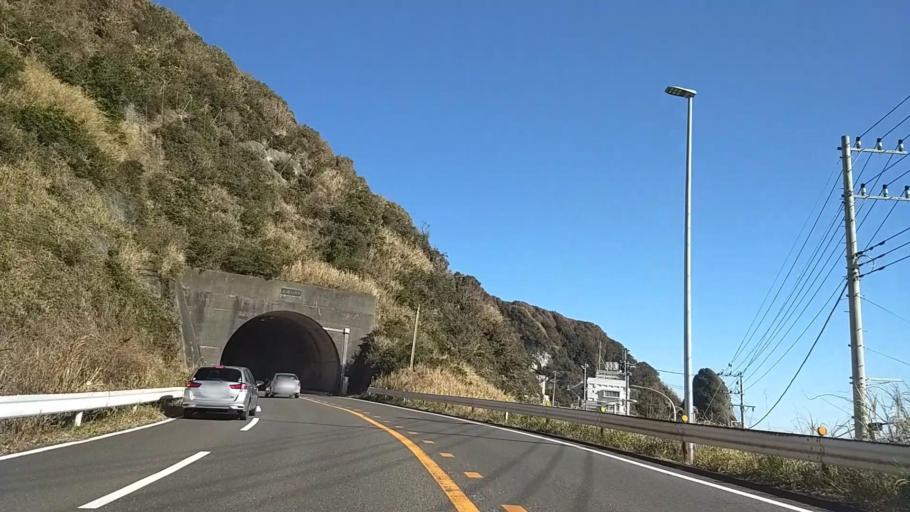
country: JP
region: Chiba
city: Kawaguchi
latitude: 35.0767
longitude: 140.0960
